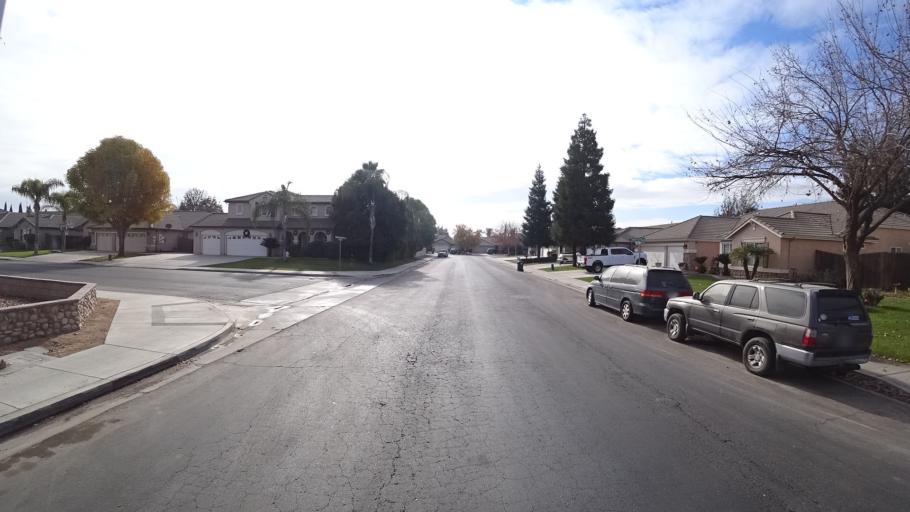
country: US
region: California
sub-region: Kern County
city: Greenacres
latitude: 35.3013
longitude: -119.1218
